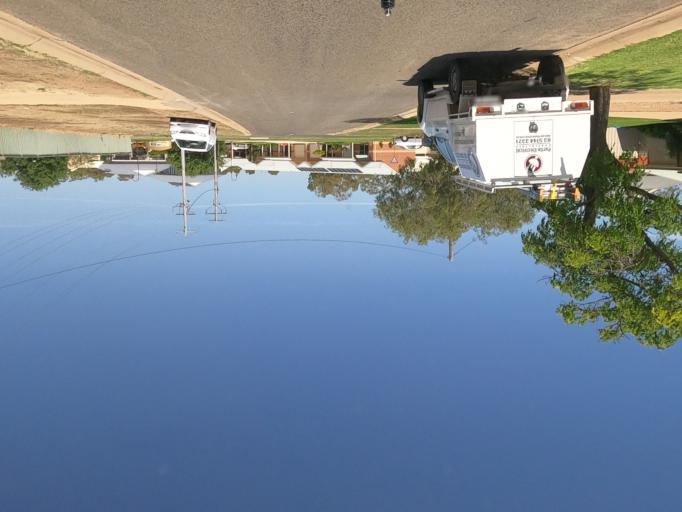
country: AU
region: New South Wales
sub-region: Corowa Shire
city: Mulwala
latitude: -35.9851
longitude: 146.0037
